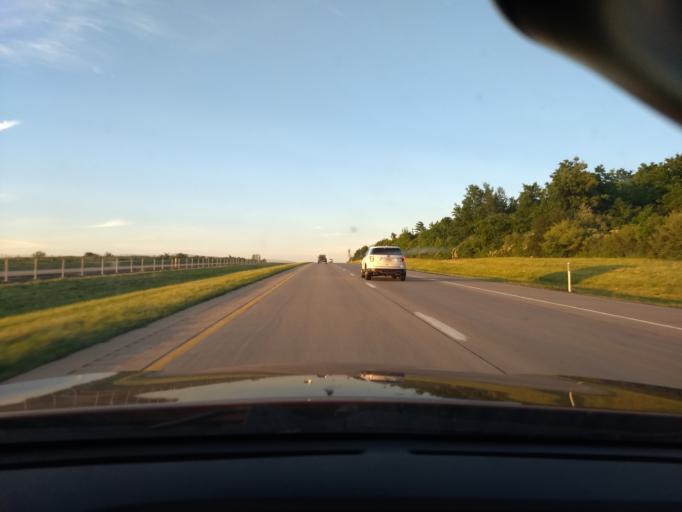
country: US
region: Pennsylvania
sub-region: Centre County
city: Houserville
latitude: 40.8512
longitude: -77.8031
